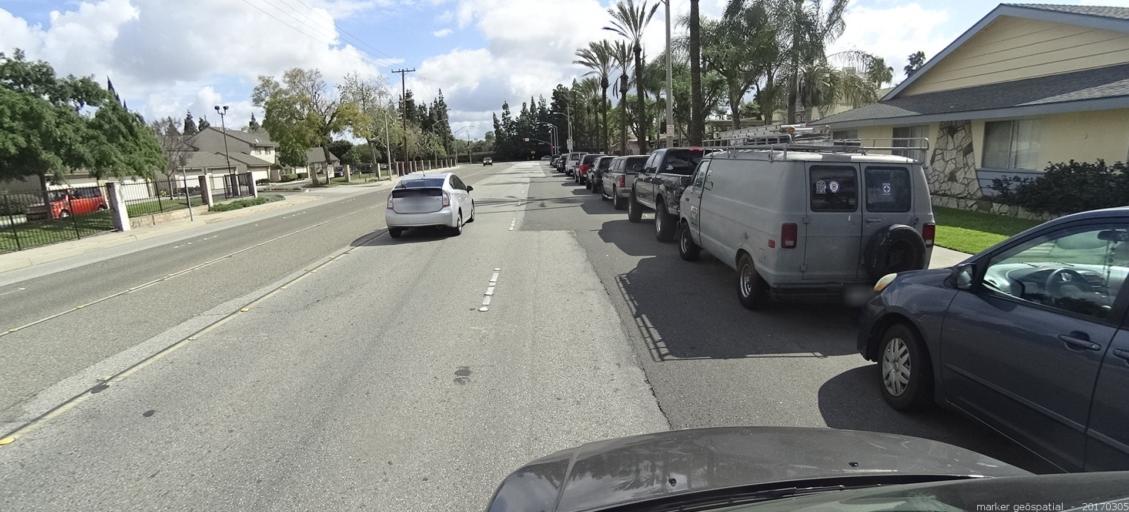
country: US
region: California
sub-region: Orange County
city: Anaheim
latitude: 33.8106
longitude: -117.9303
